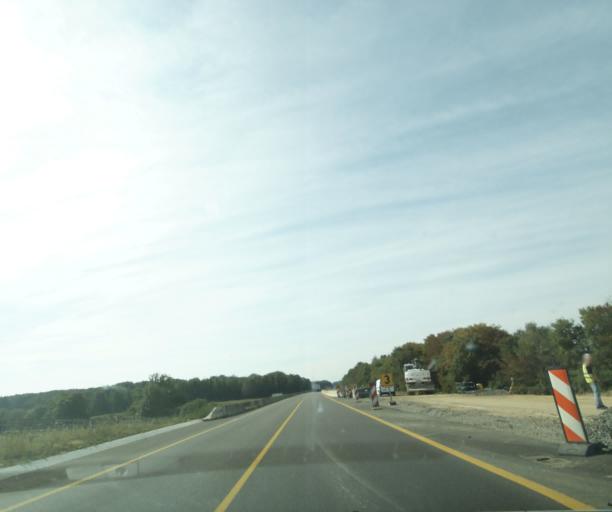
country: FR
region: Bourgogne
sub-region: Departement de Saone-et-Loire
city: Paray-le-Monial
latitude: 46.4958
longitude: 4.1577
